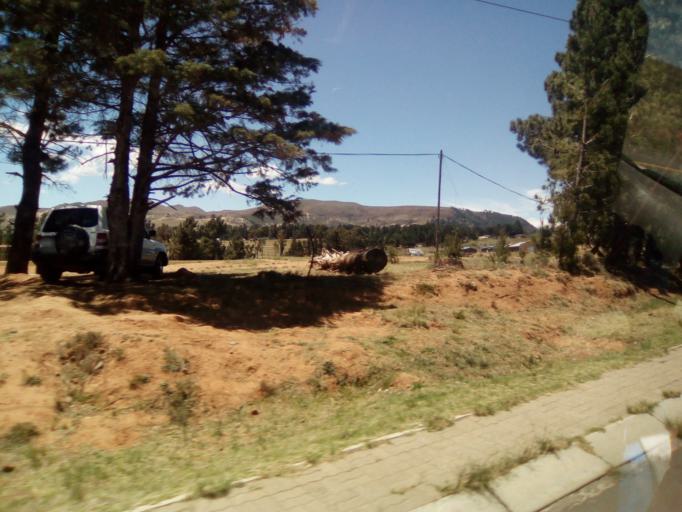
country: LS
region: Qacha's Nek
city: Qacha's Nek
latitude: -30.1087
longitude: 28.6708
